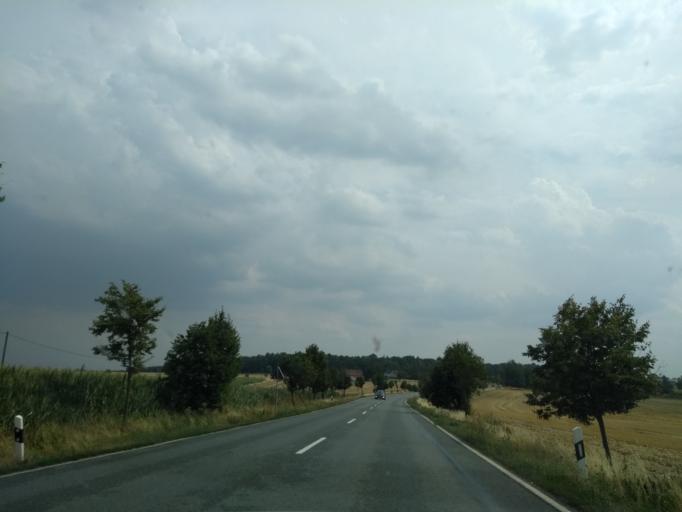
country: DE
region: Thuringia
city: Hirschfeld
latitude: 50.9743
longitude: 12.1347
